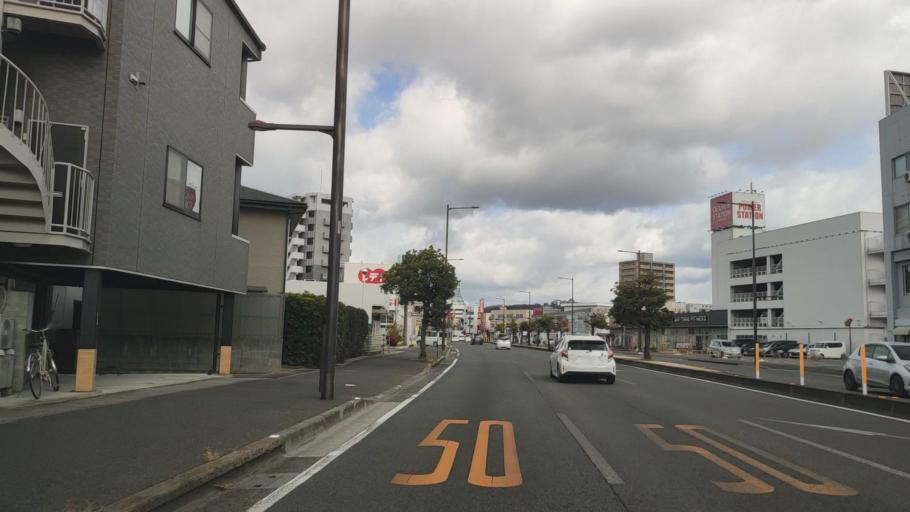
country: JP
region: Ehime
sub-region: Shikoku-chuo Shi
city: Matsuyama
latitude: 33.8263
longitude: 132.7587
